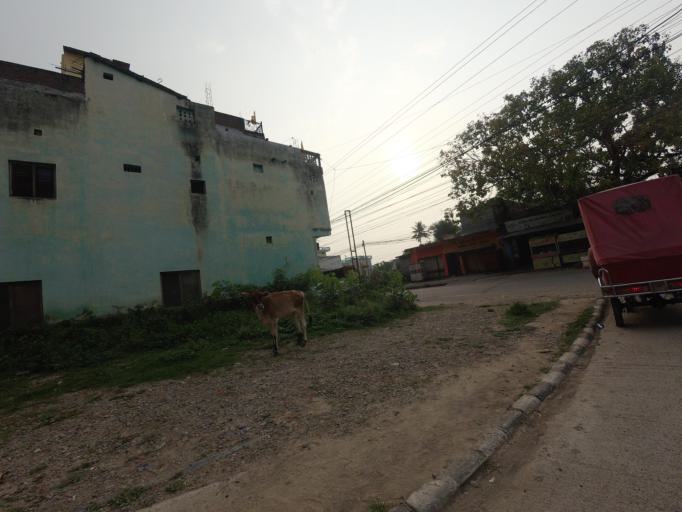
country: NP
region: Western Region
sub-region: Lumbini Zone
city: Bhairahawa
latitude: 27.5010
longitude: 83.4488
